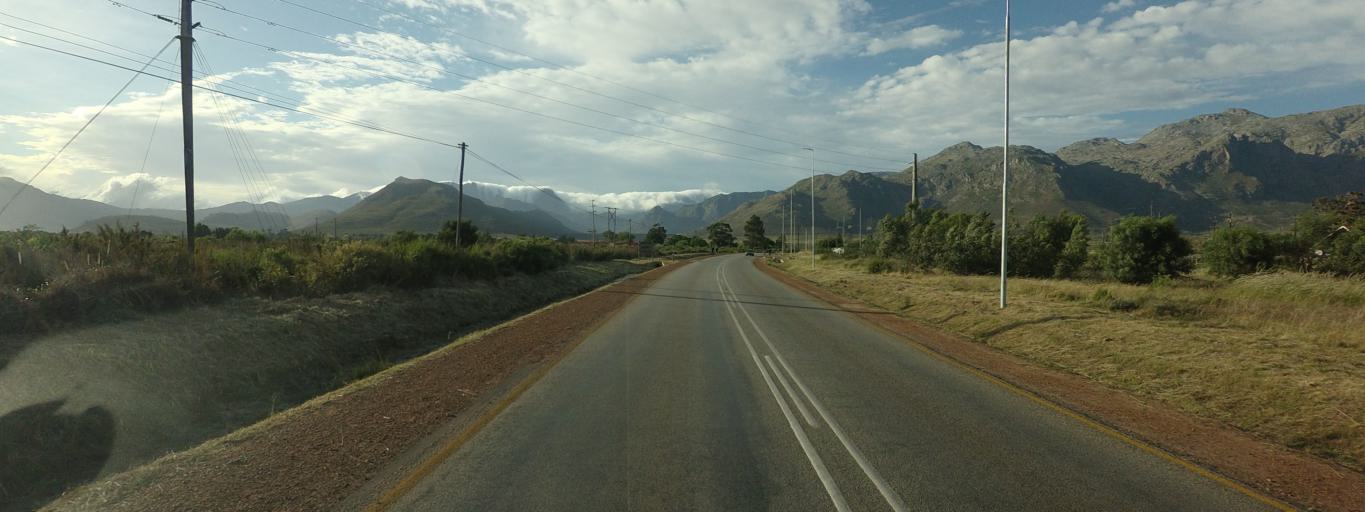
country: ZA
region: Western Cape
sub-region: Cape Winelands District Municipality
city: Paarl
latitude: -33.8738
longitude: 19.0446
